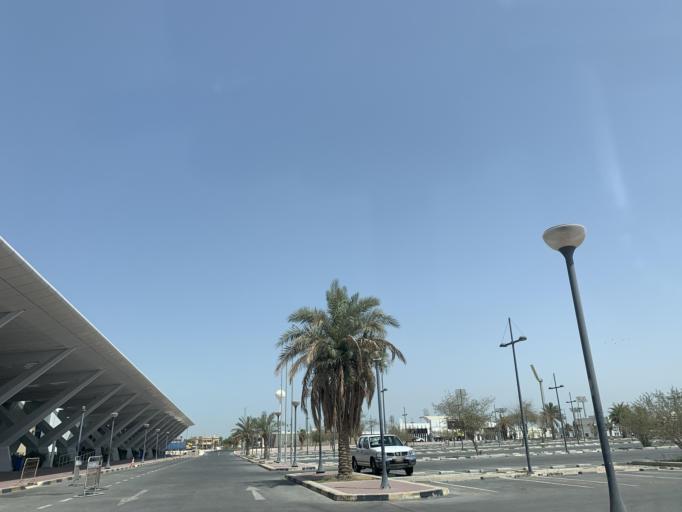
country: BH
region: Northern
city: Madinat `Isa
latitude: 26.1555
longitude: 50.5440
